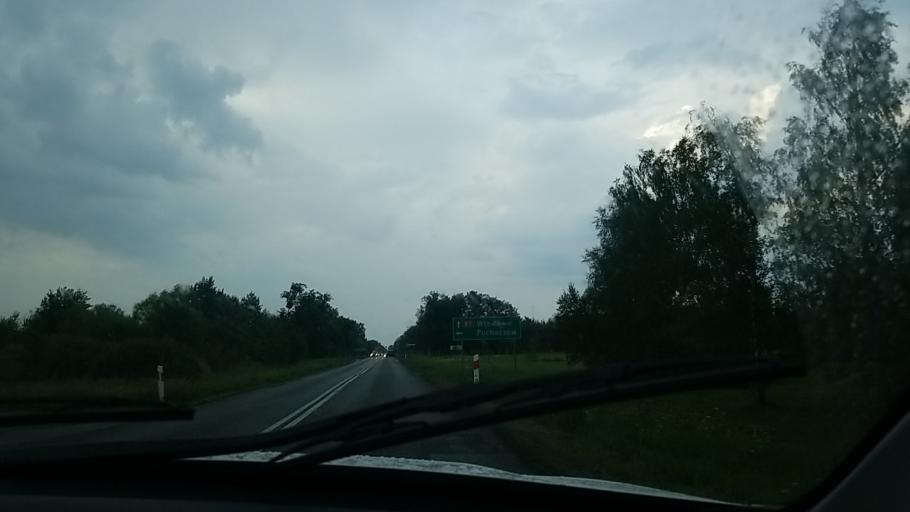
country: PL
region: Lublin Voivodeship
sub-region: Powiat wlodawski
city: Urszulin
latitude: 51.3837
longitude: 23.1890
